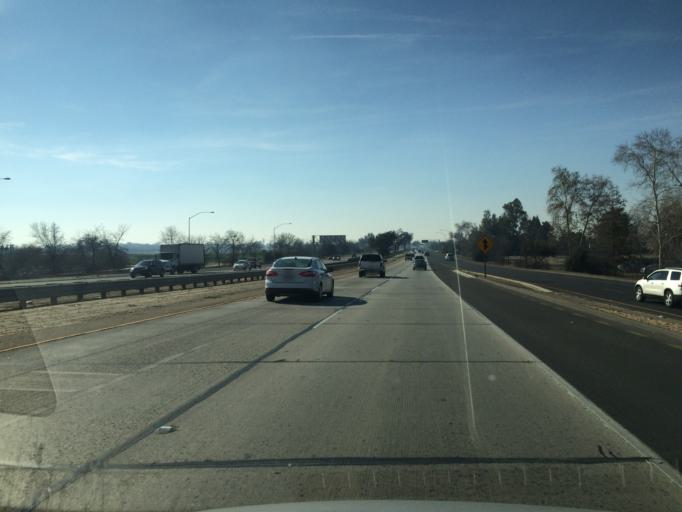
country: US
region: California
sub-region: Tulare County
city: Visalia
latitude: 36.3274
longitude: -119.3518
